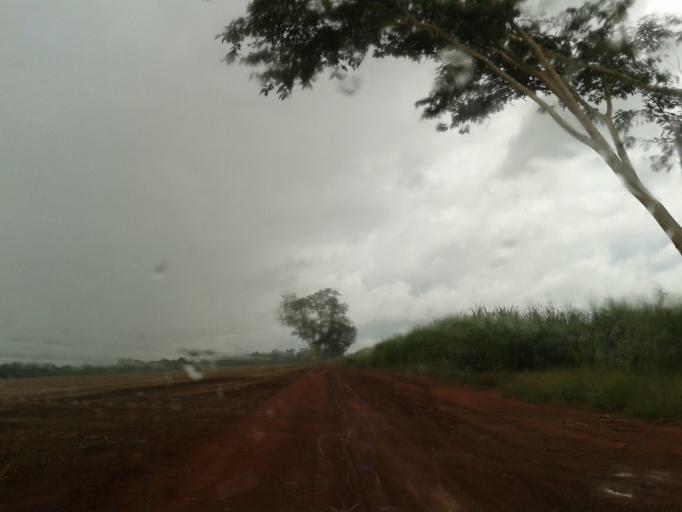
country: BR
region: Minas Gerais
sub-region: Santa Vitoria
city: Santa Vitoria
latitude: -18.6585
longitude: -49.9111
